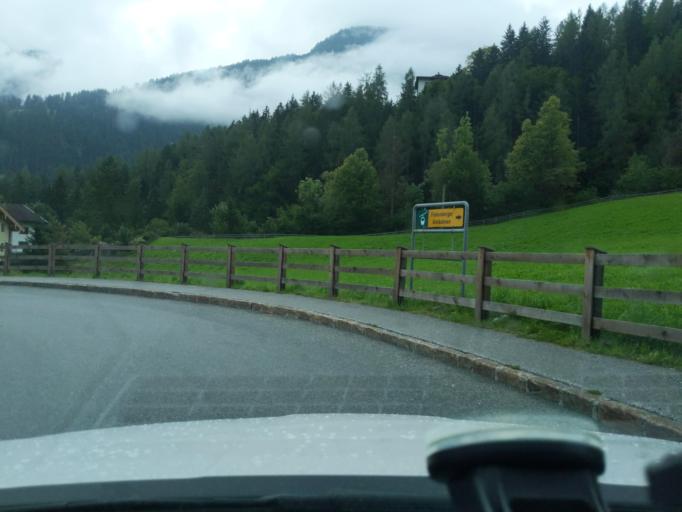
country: AT
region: Tyrol
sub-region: Politischer Bezirk Schwaz
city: Mayrhofen
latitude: 47.1531
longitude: 11.8234
